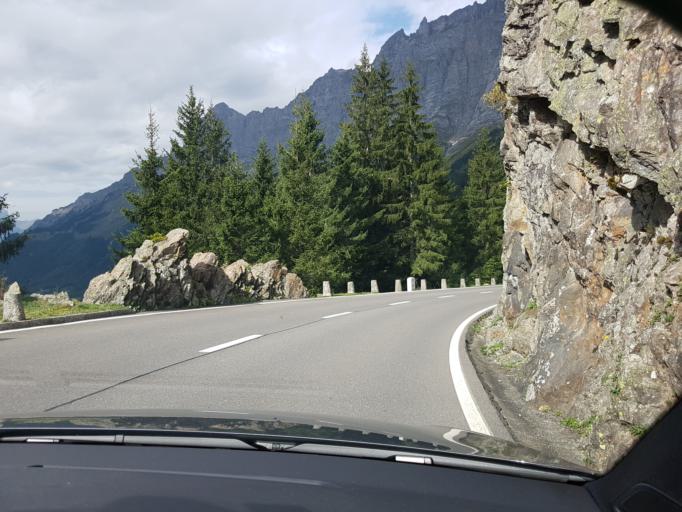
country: CH
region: Obwalden
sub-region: Obwalden
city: Engelberg
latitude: 46.7390
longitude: 8.3841
